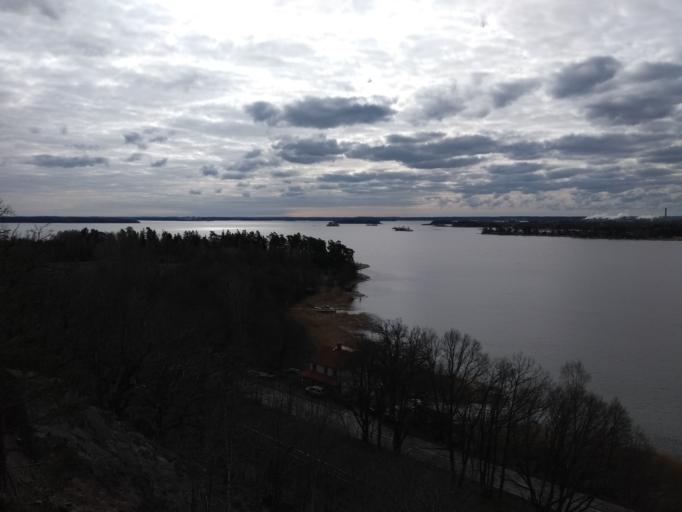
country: SE
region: OEstergoetland
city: Lindo
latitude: 58.6658
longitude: 16.2539
